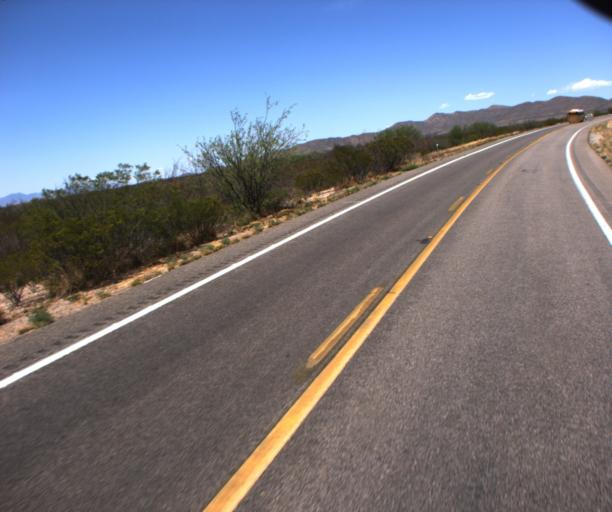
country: US
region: Arizona
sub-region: Cochise County
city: Tombstone
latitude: 31.6154
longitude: -110.0520
